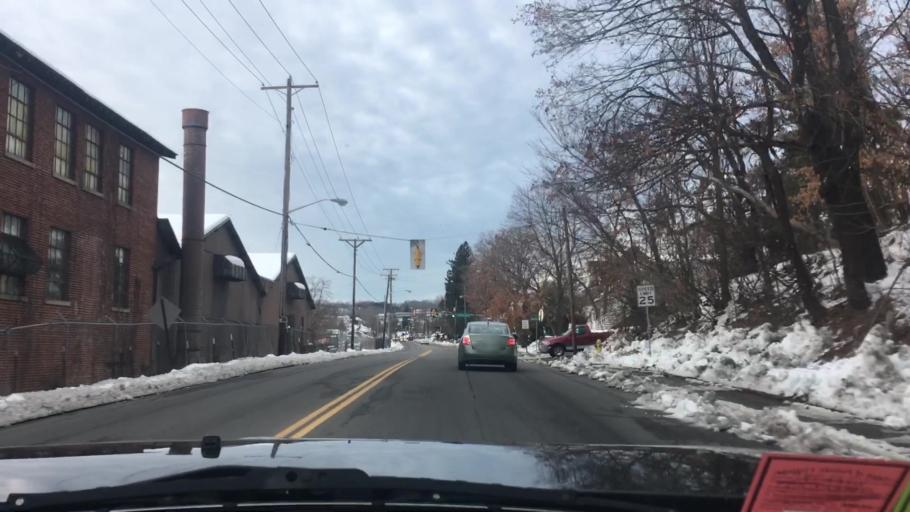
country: US
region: Virginia
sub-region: Pulaski County
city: Pulaski
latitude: 37.0513
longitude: -80.7756
